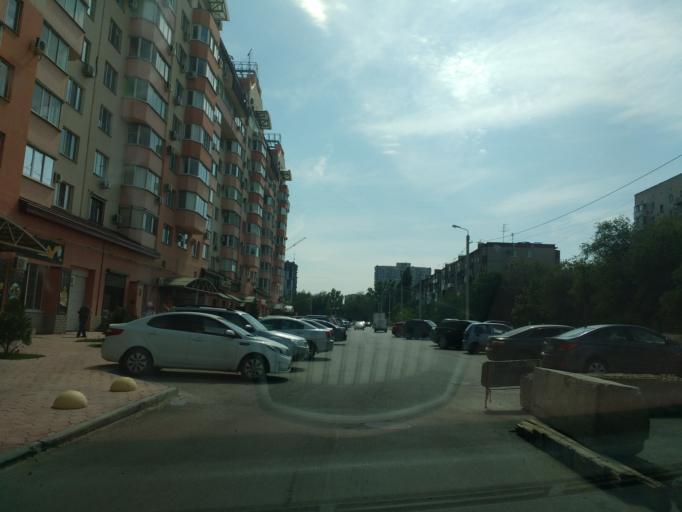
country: RU
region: Volgograd
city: Volgograd
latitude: 48.6899
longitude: 44.4928
